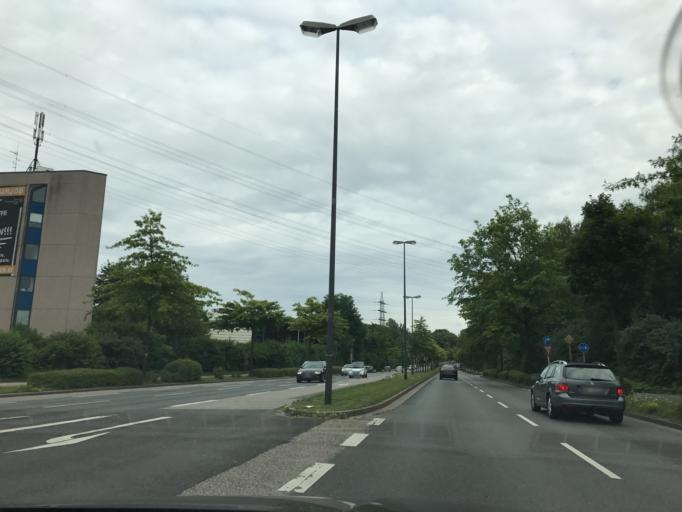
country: DE
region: North Rhine-Westphalia
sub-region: Regierungsbezirk Dusseldorf
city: Essen
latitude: 51.4719
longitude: 6.9919
